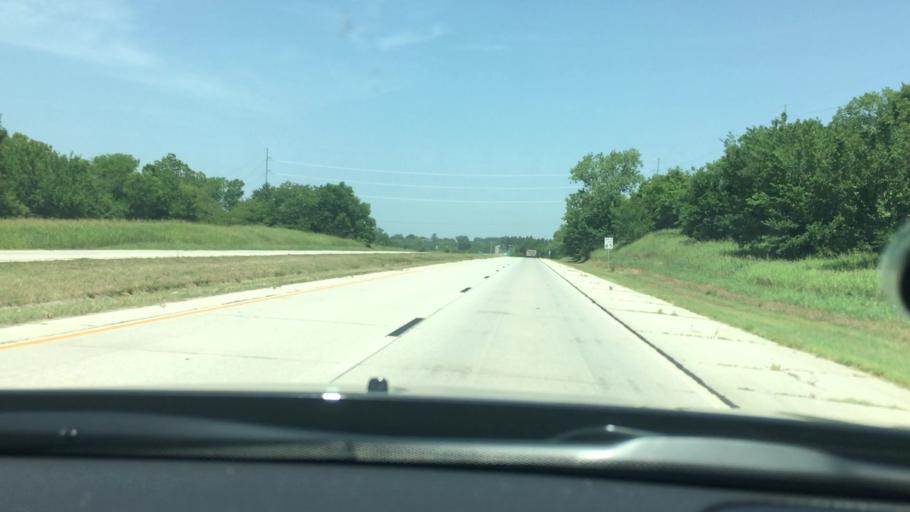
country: US
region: Oklahoma
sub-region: Pontotoc County
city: Ada
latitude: 34.7503
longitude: -96.6582
